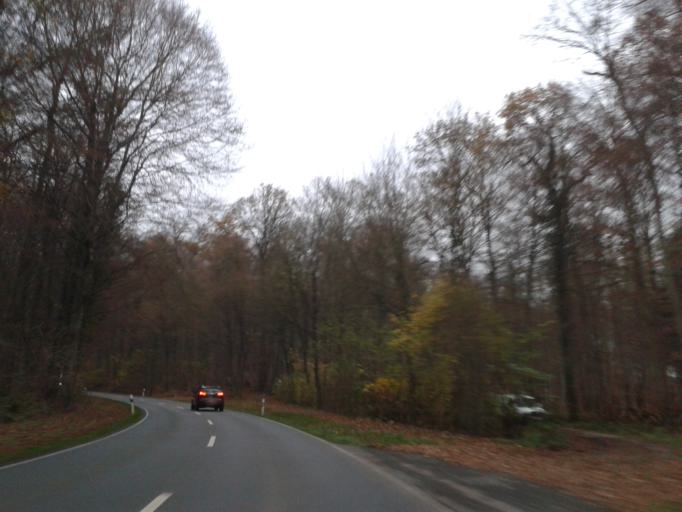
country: DE
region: North Rhine-Westphalia
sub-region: Regierungsbezirk Detmold
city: Blomberg
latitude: 51.9292
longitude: 9.1495
